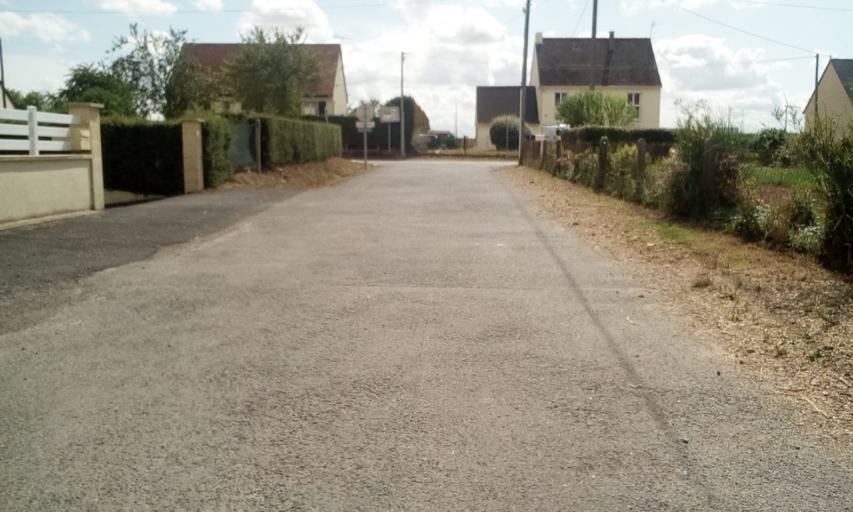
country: FR
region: Lower Normandy
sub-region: Departement du Calvados
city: Bellengreville
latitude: 49.1087
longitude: -0.2110
